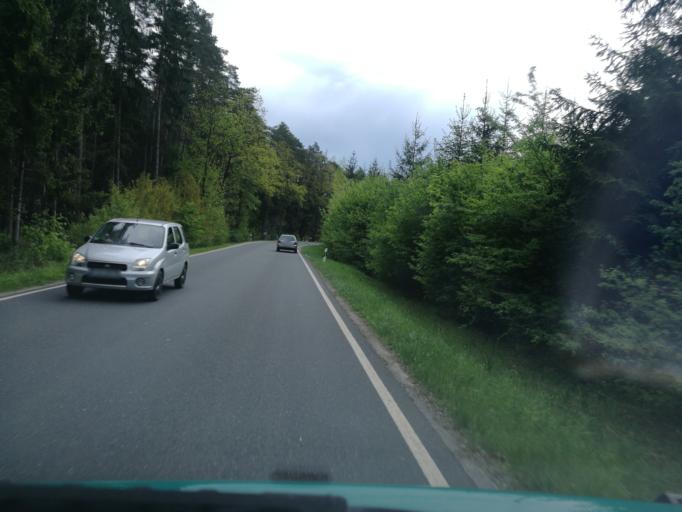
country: DE
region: Bavaria
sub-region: Upper Franconia
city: Michelau
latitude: 50.1928
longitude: 11.1104
